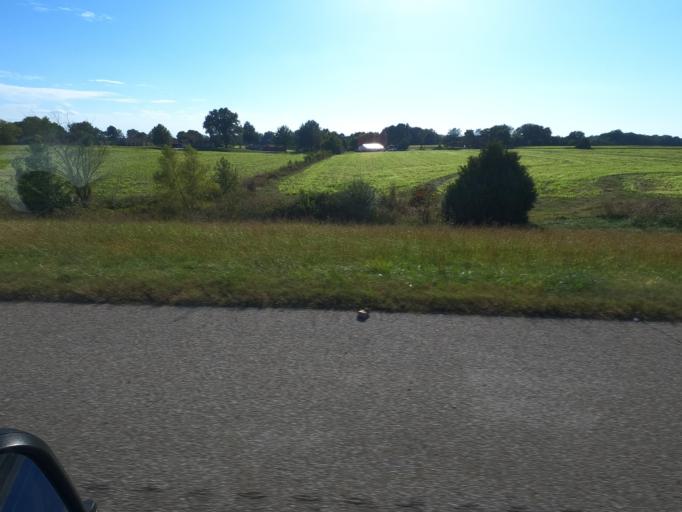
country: US
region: Tennessee
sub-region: Crockett County
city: Alamo
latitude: 35.7839
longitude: -89.1457
